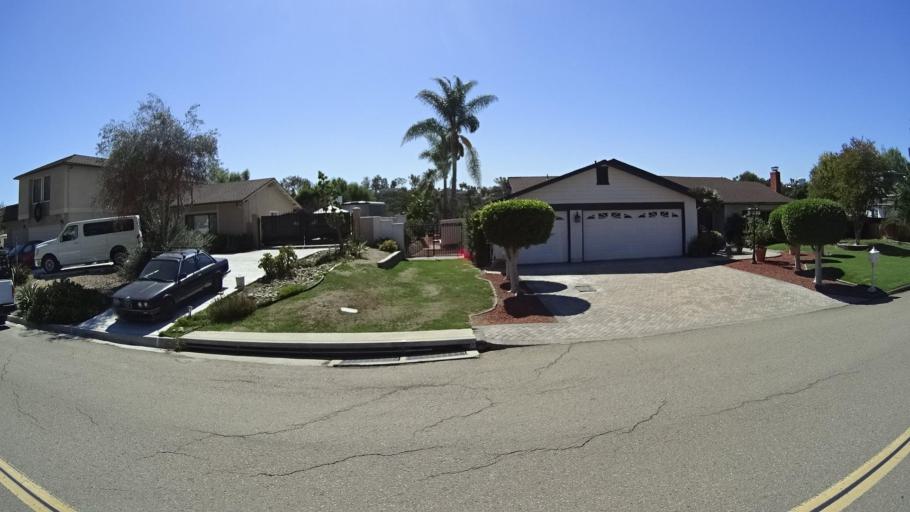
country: US
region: California
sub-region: San Diego County
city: Bonita
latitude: 32.6596
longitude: -117.0167
